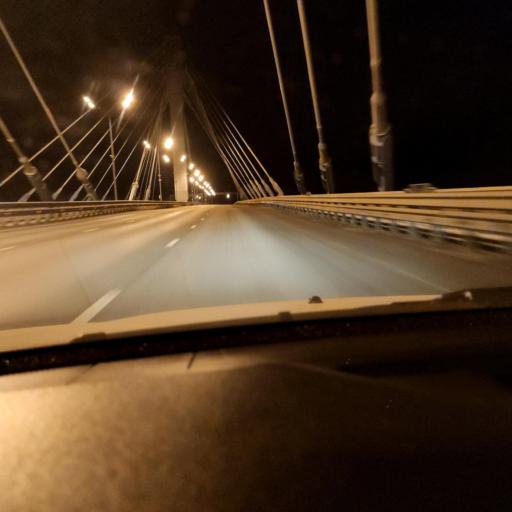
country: RU
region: Samara
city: Smyshlyayevka
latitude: 53.1800
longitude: 50.3068
